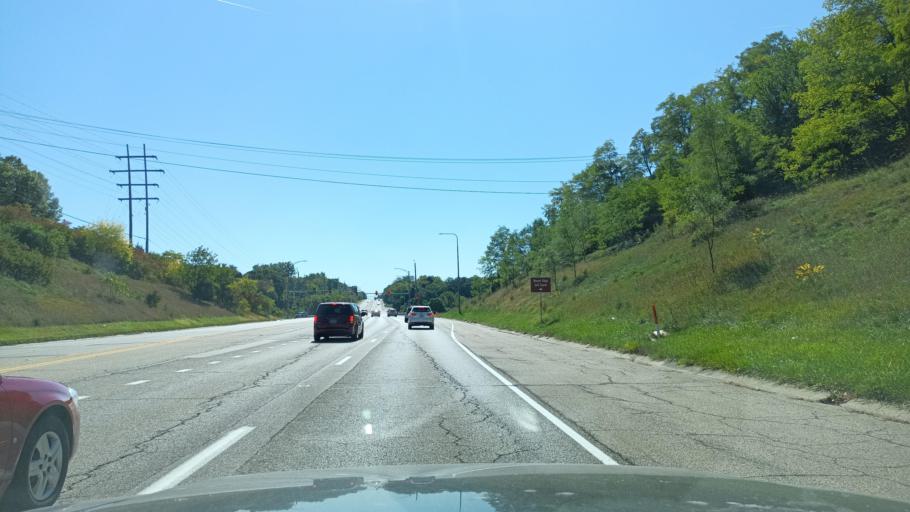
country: US
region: Illinois
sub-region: Peoria County
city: Peoria Heights
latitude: 40.7615
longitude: -89.6398
